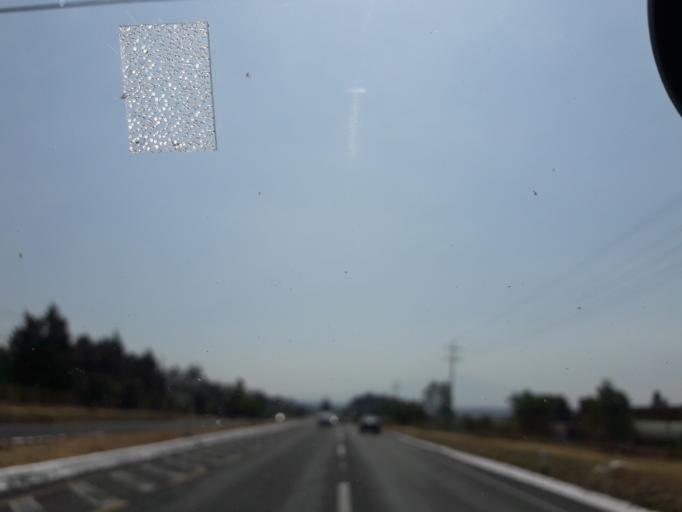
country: MX
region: Tlaxcala
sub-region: Panotla
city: Fraccionamiento la Virgen
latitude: 19.3221
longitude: -98.2725
